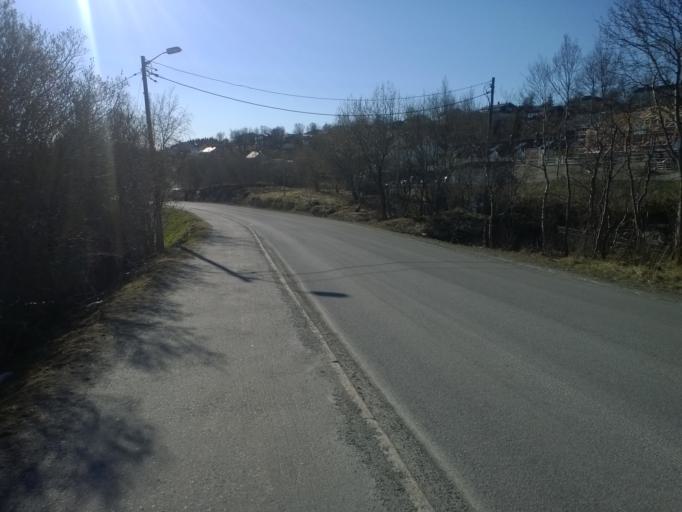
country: NO
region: Nordland
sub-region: Bodo
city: Lopsmarka
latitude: 67.2779
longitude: 14.5090
